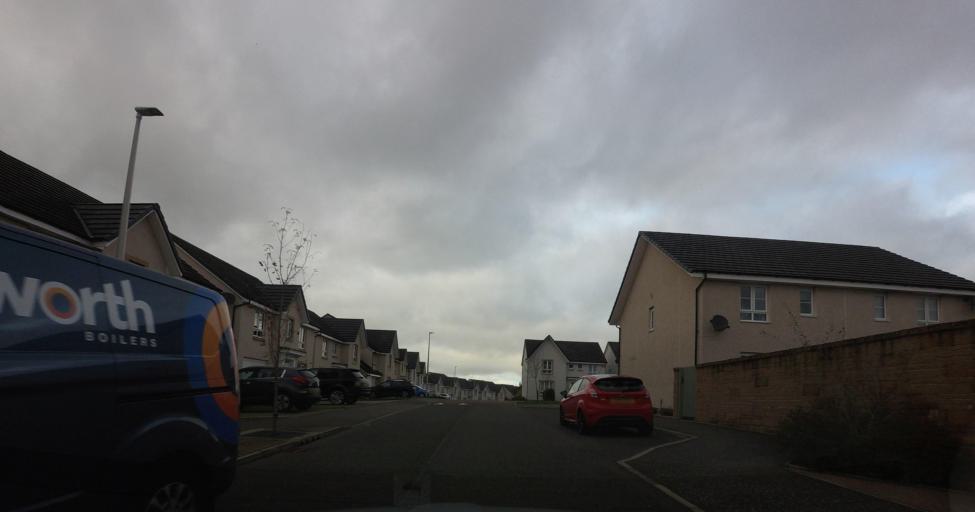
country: GB
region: Scotland
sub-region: West Lothian
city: Bathgate
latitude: 55.8864
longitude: -3.6517
